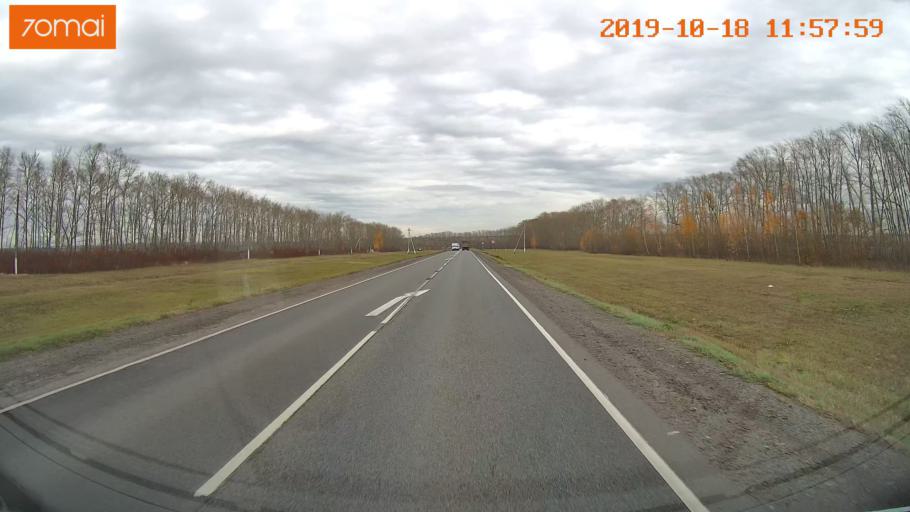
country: RU
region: Rjazan
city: Mikhaylov
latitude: 54.2682
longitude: 39.1578
